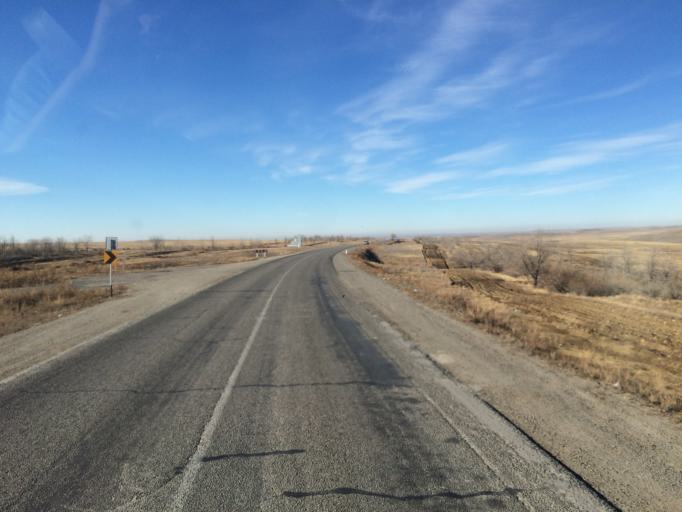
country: KZ
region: Aqtoebe
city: Aqtobe
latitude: 50.2818
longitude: 57.7489
